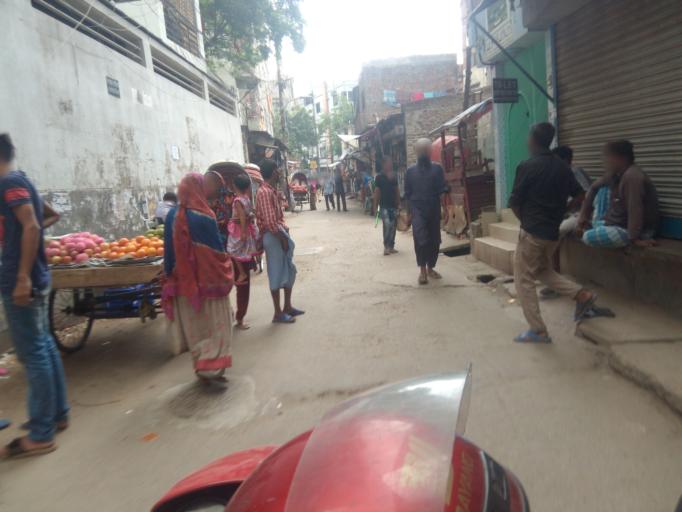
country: BD
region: Dhaka
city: Azimpur
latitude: 23.7230
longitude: 90.3810
